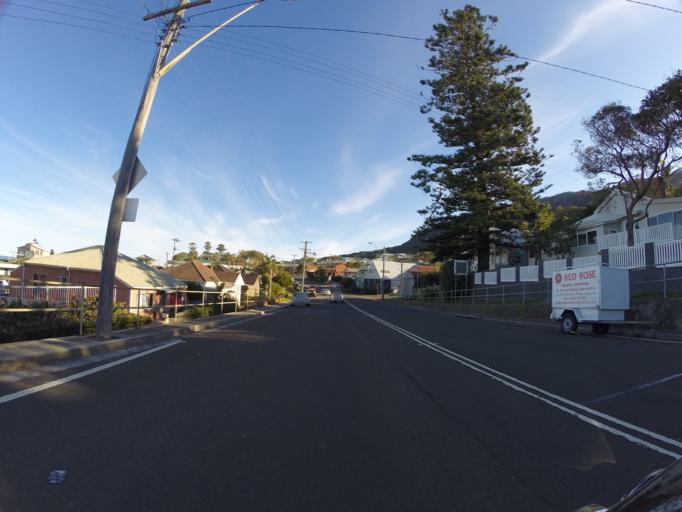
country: AU
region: New South Wales
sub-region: Wollongong
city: Bulli
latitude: -34.2899
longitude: 150.9458
